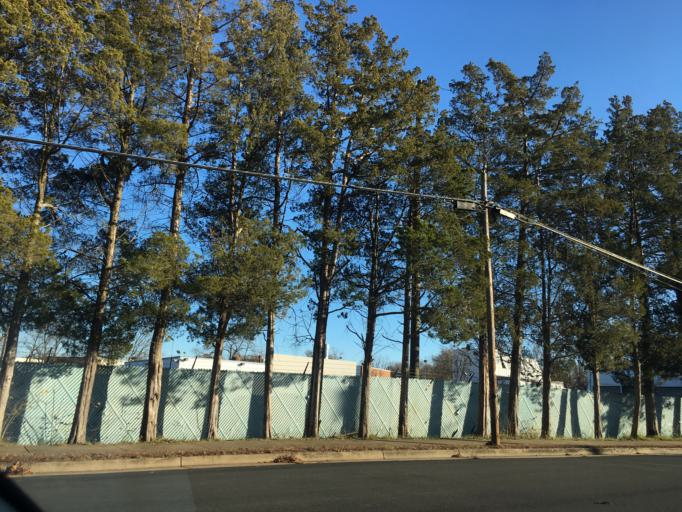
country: US
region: Virginia
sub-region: City of Fairfax
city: Fairfax
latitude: 38.8584
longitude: -77.3119
